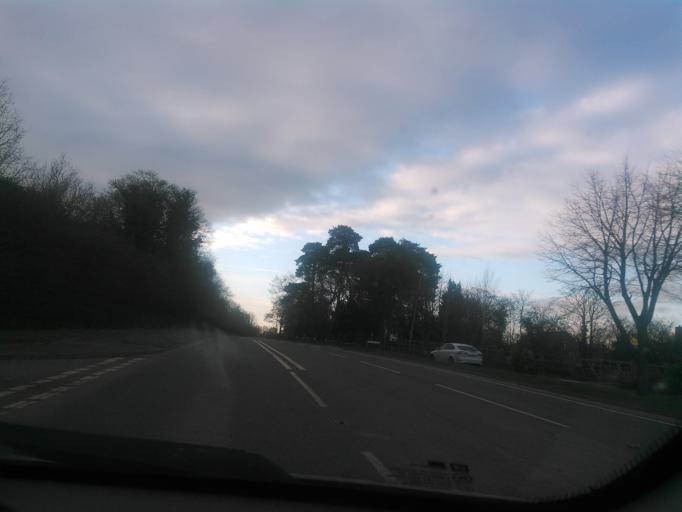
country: GB
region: England
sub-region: Shropshire
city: Market Drayton
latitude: 52.8415
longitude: -2.4653
